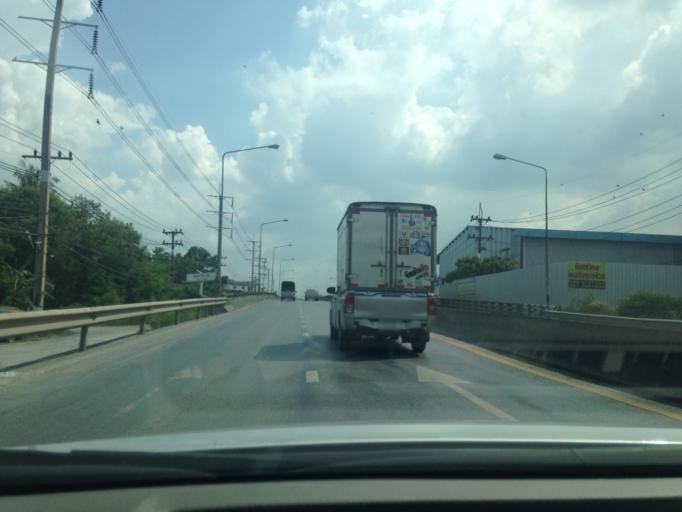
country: TH
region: Pathum Thani
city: Sam Khok
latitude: 14.0775
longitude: 100.5208
